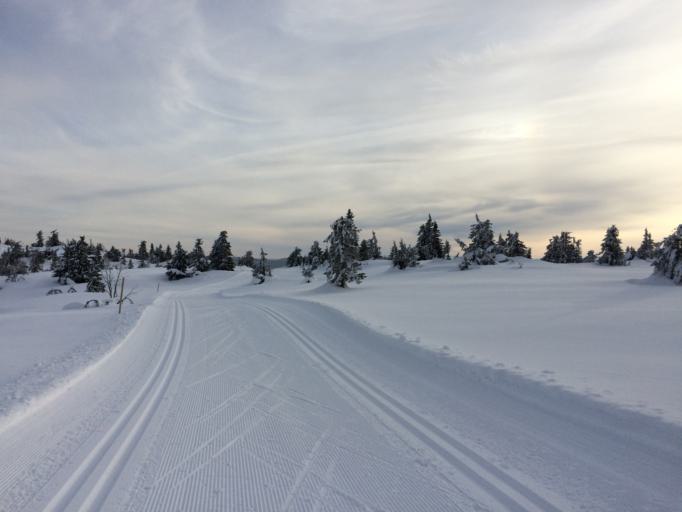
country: NO
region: Oppland
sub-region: Gausdal
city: Segalstad bru
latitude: 61.3237
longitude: 10.0410
